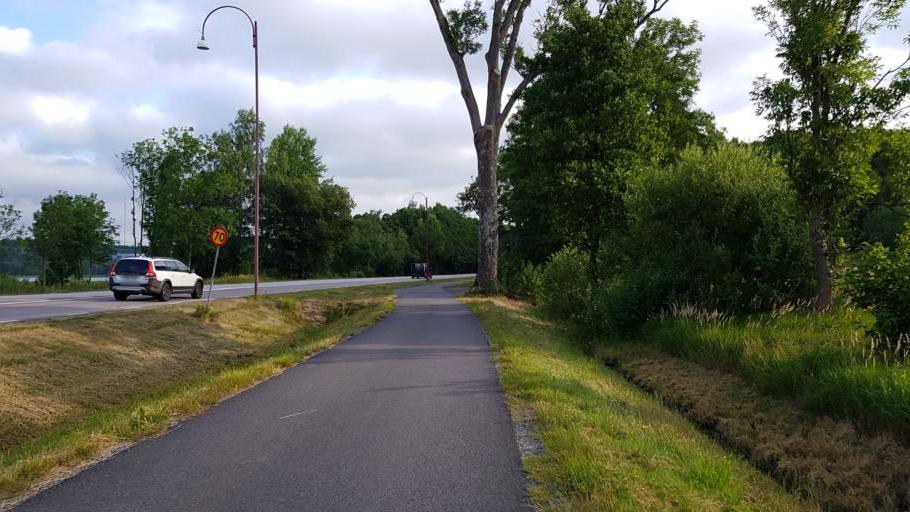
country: SE
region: Vaestra Goetaland
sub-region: Harryda Kommun
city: Molnlycke
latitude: 57.6625
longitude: 12.0922
